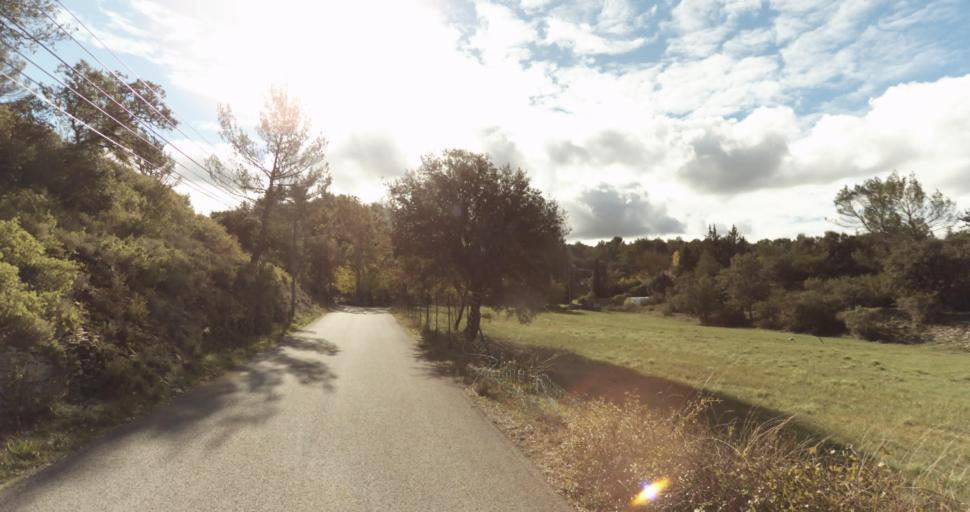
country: FR
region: Provence-Alpes-Cote d'Azur
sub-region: Departement des Bouches-du-Rhone
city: Venelles
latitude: 43.5864
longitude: 5.5071
